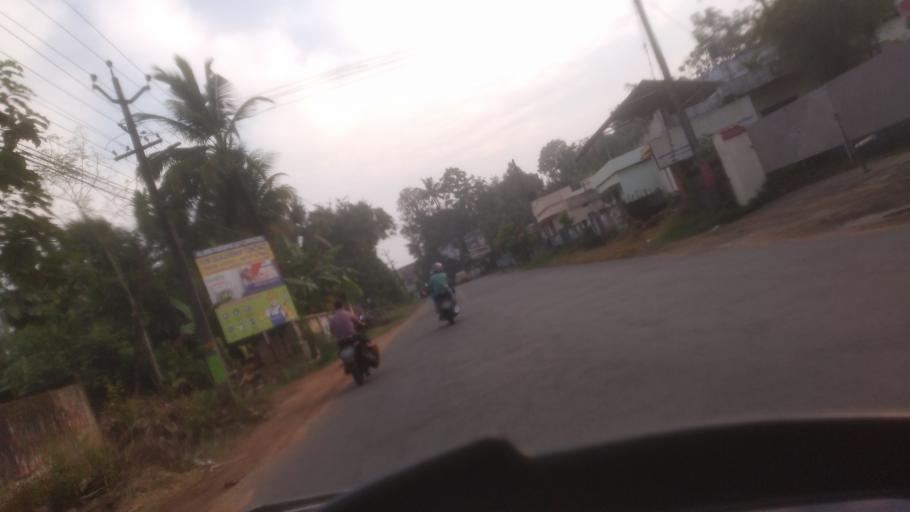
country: IN
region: Kerala
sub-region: Ernakulam
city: Perumbavoor
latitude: 10.1155
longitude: 76.4298
